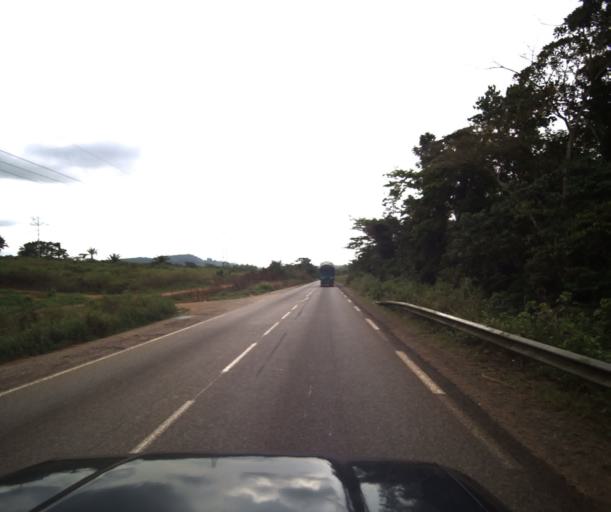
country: CM
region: Littoral
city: Edea
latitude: 3.8164
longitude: 10.3409
